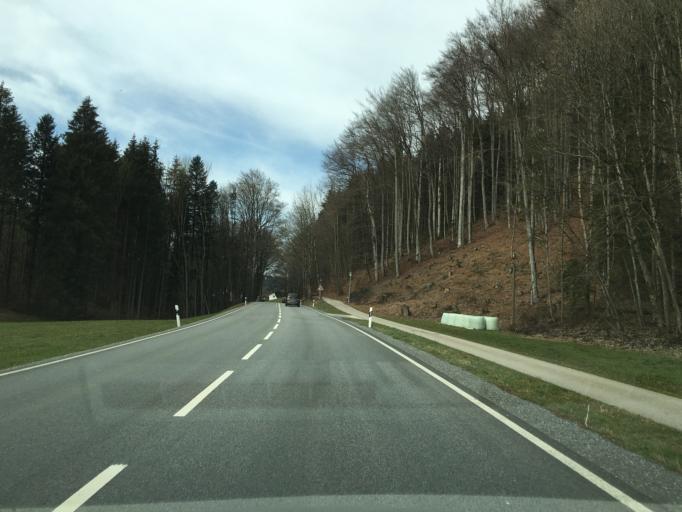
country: DE
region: Bavaria
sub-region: Upper Bavaria
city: Inzell
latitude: 47.7976
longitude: 12.7162
